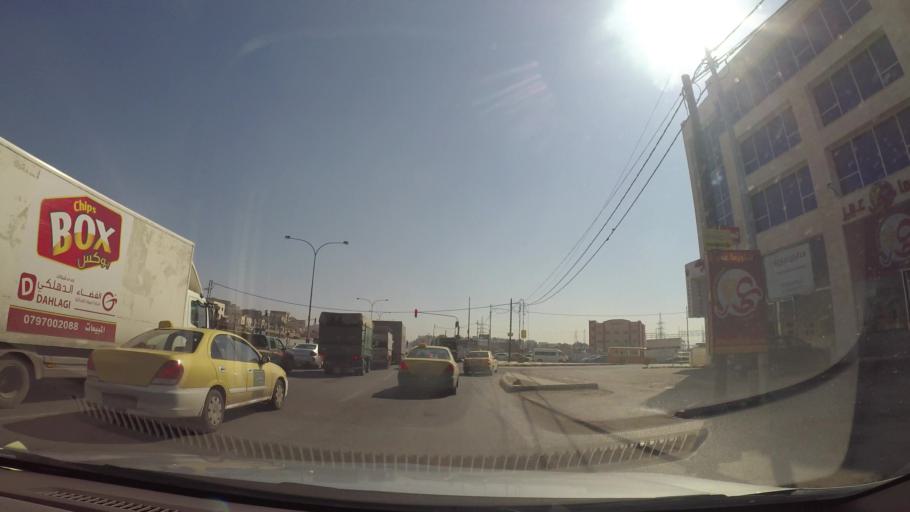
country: JO
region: Amman
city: Al Bunayyat ash Shamaliyah
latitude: 31.8962
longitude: 35.9034
